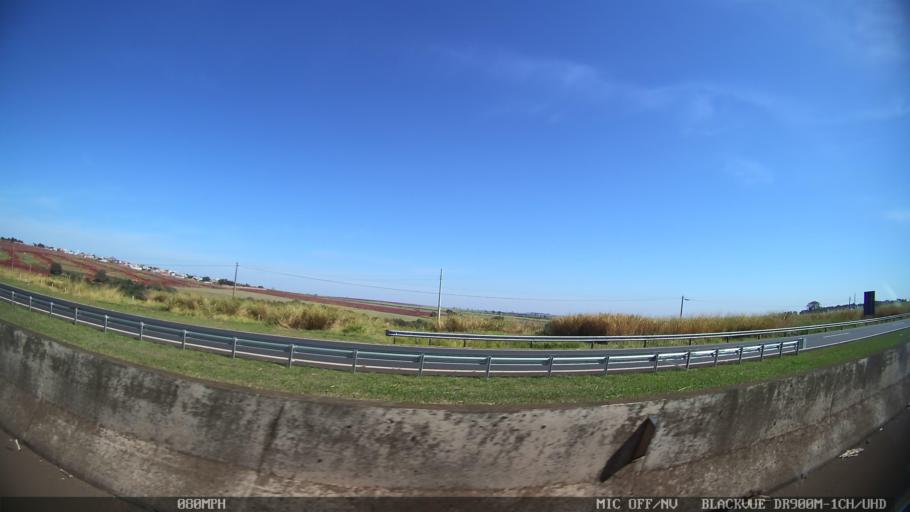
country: BR
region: Sao Paulo
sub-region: Cravinhos
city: Cravinhos
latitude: -21.3083
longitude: -47.7386
